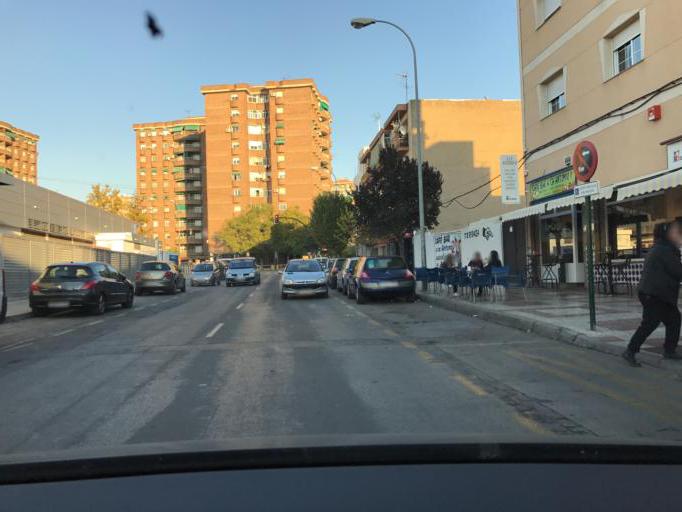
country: ES
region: Andalusia
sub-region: Provincia de Granada
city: Granada
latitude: 37.1967
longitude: -3.6051
